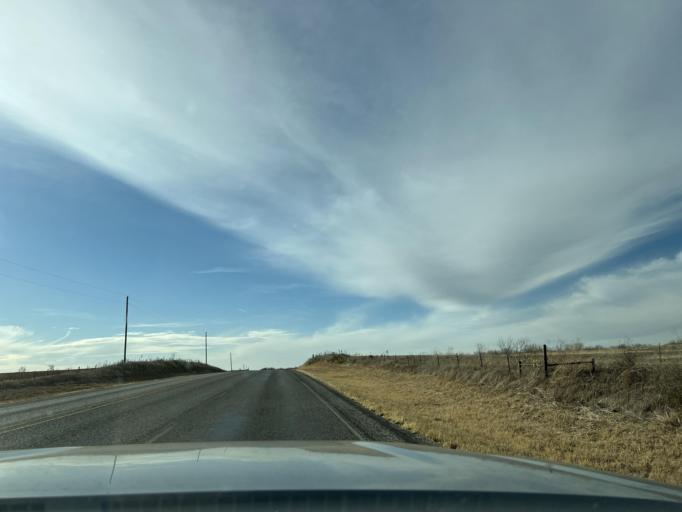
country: US
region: Texas
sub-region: Fisher County
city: Rotan
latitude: 32.7393
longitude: -100.5348
